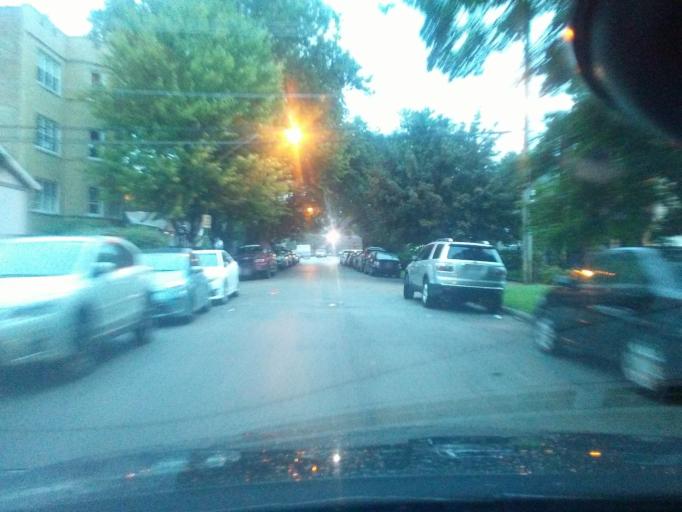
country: US
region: Illinois
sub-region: Cook County
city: Evanston
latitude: 41.9982
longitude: -87.6724
